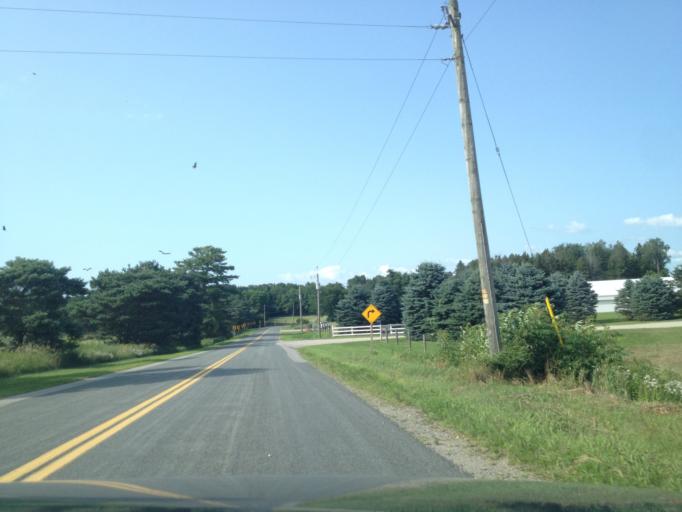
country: CA
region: Ontario
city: Aylmer
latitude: 42.7435
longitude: -80.8532
